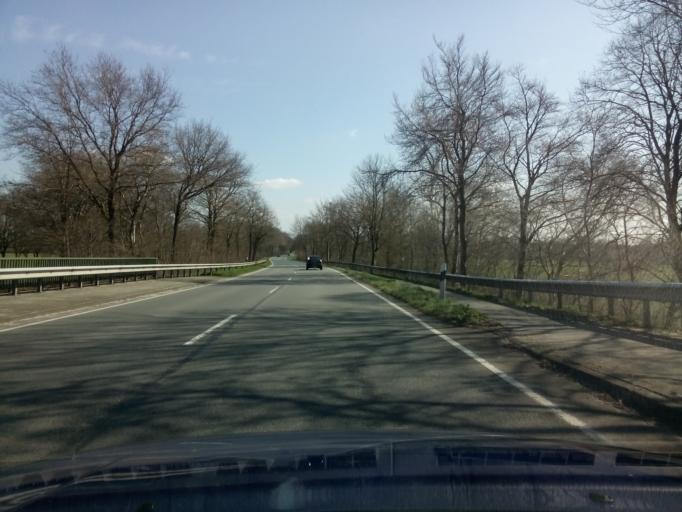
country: DE
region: Lower Saxony
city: Emlichheim
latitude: 52.6196
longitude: 6.7940
